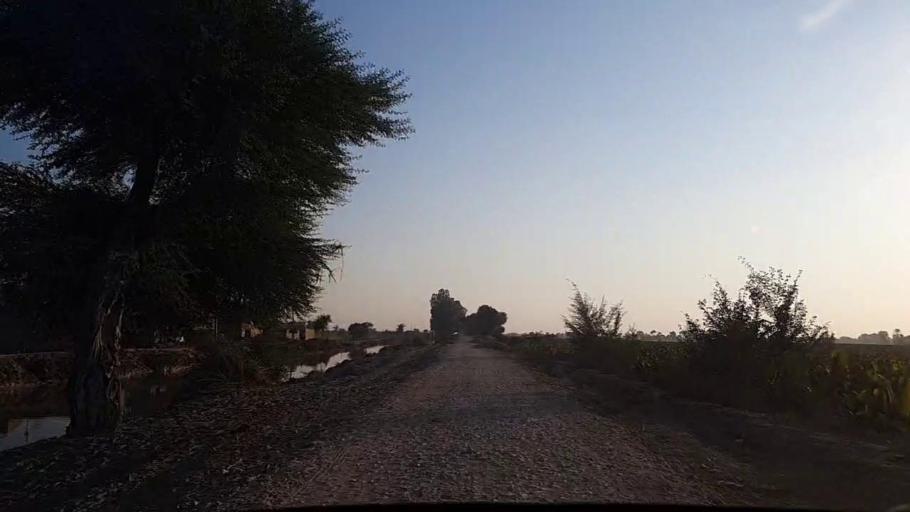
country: PK
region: Sindh
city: Sobhadero
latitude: 27.3858
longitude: 68.3823
